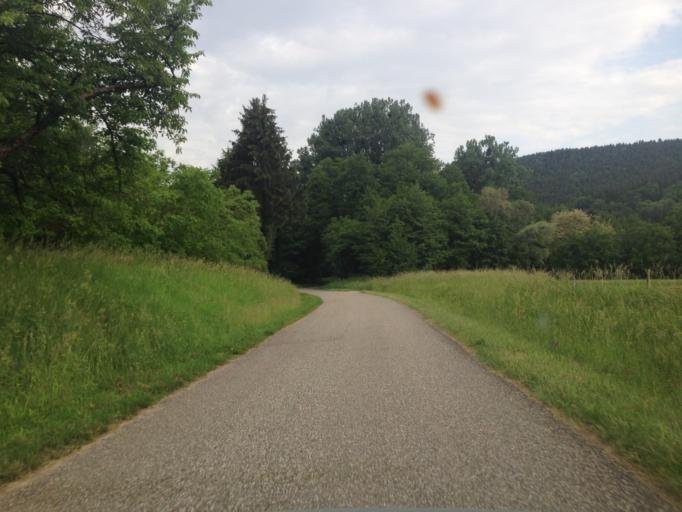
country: FR
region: Alsace
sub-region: Departement du Bas-Rhin
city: Neuwiller-les-Saverne
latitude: 48.8300
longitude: 7.4016
